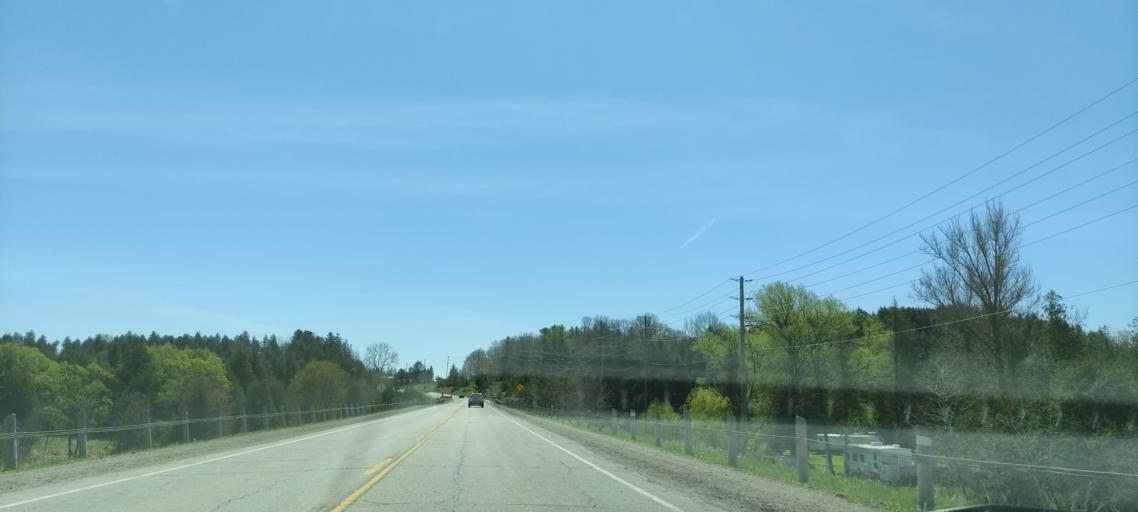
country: CA
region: Ontario
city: Waterloo
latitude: 43.5893
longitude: -80.4728
